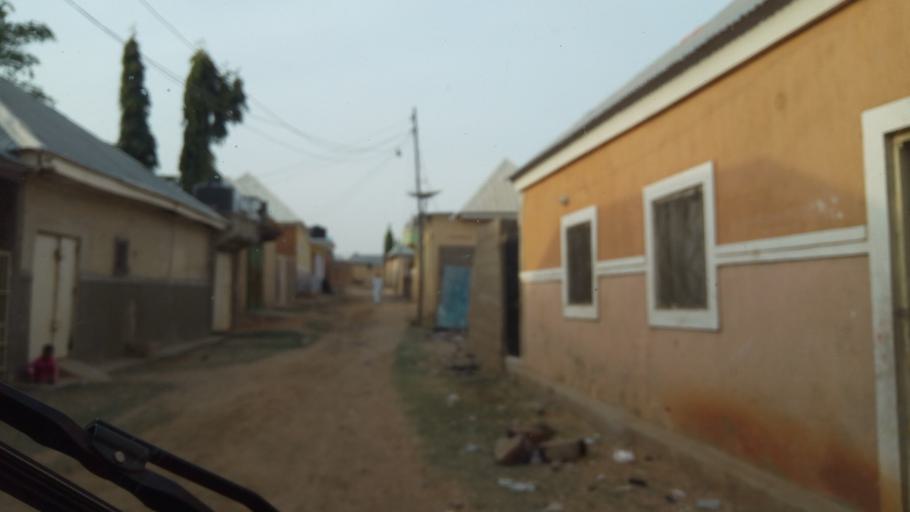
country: NG
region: Gombe
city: Gombe
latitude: 10.2575
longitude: 11.1855
